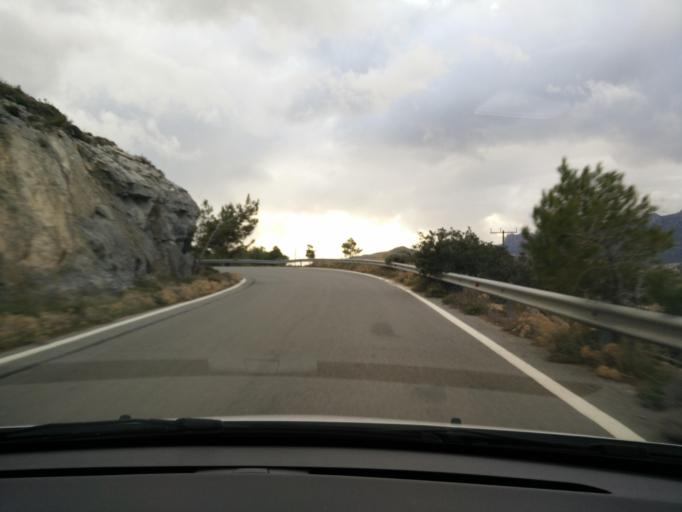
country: GR
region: Crete
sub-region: Nomos Lasithiou
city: Gra Liyia
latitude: 35.0759
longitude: 25.7037
